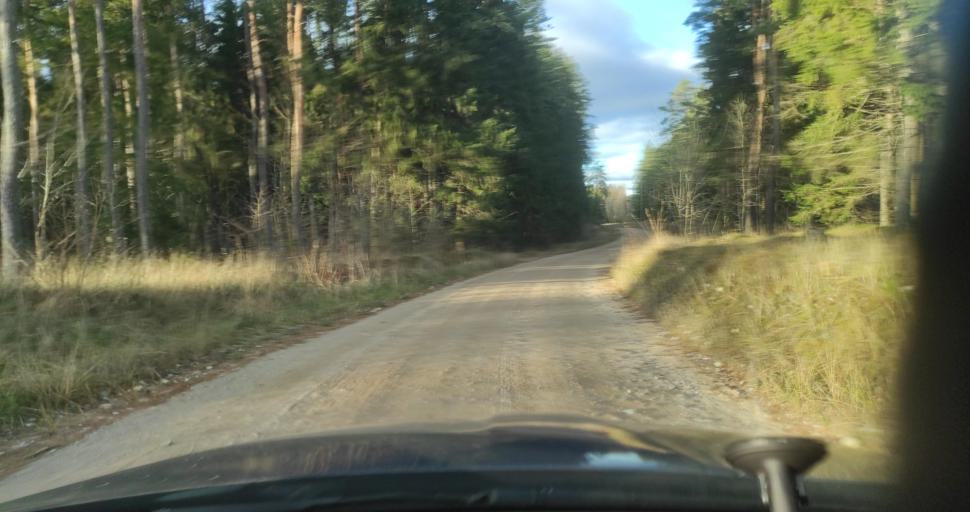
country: LV
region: Kuldigas Rajons
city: Kuldiga
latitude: 57.2834
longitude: 22.0394
